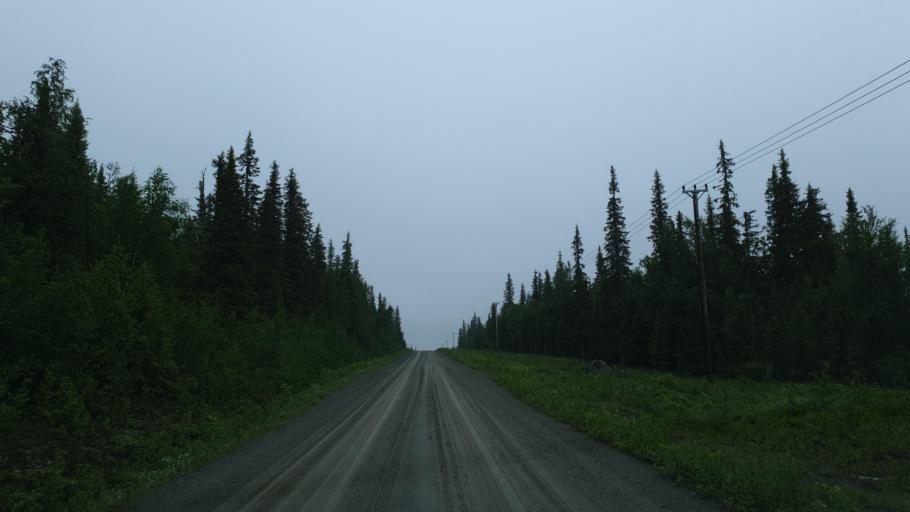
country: SE
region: Vaesterbotten
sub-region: Vilhelmina Kommun
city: Sjoberg
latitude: 65.3182
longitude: 15.9476
